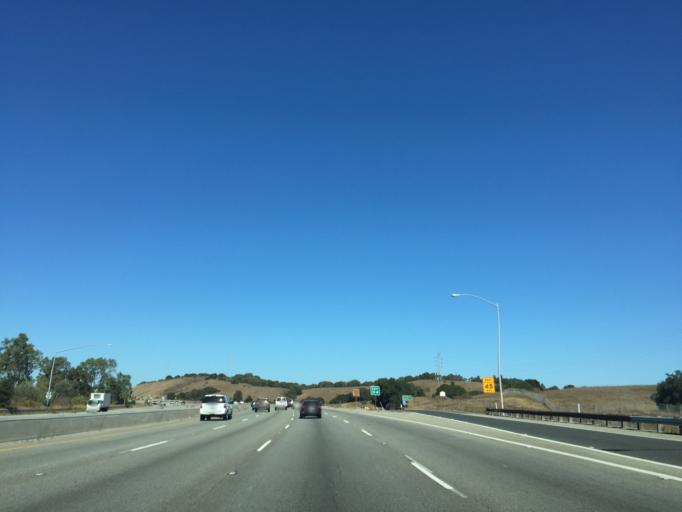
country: US
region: California
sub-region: San Mateo County
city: Emerald Lake Hills
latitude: 37.4659
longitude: -122.2910
